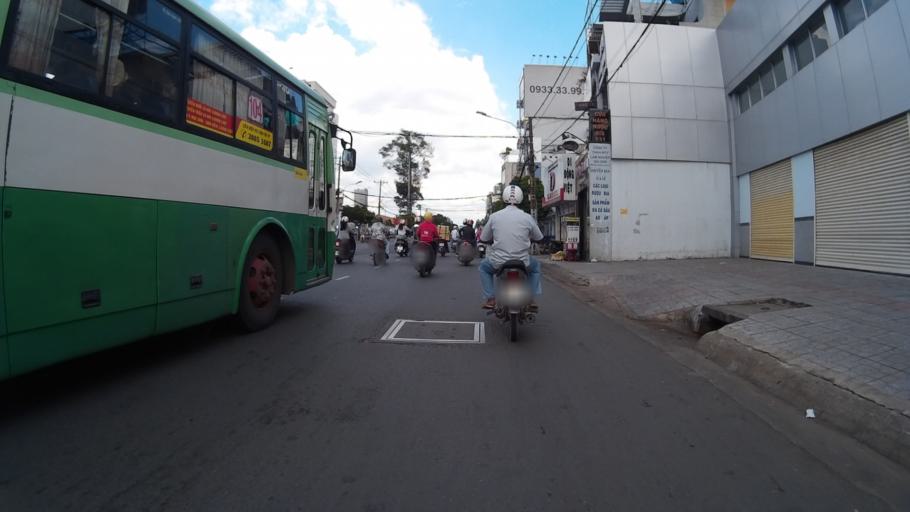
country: VN
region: Ho Chi Minh City
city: Quan Phu Nhuan
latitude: 10.8000
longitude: 106.6688
